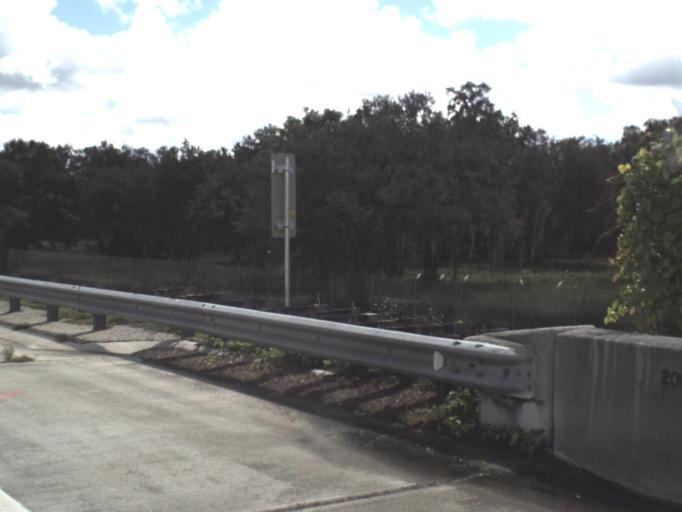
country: US
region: Florida
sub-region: DeSoto County
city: Arcadia
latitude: 27.2567
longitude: -81.9713
